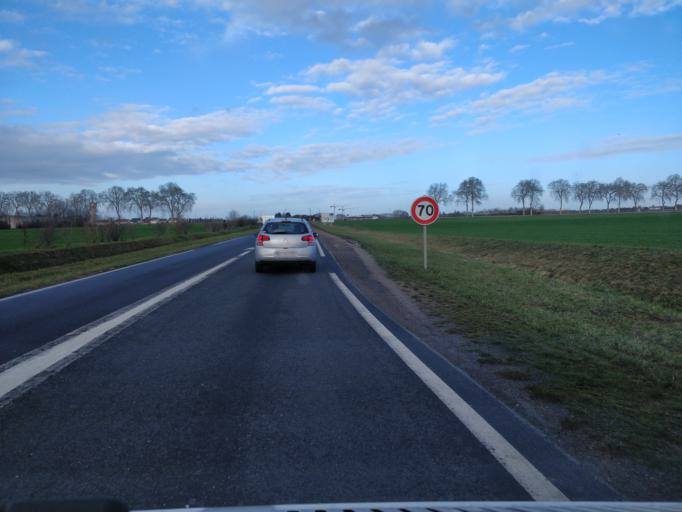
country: FR
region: Centre
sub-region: Departement du Loir-et-Cher
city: Mer
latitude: 47.7043
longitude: 1.5232
